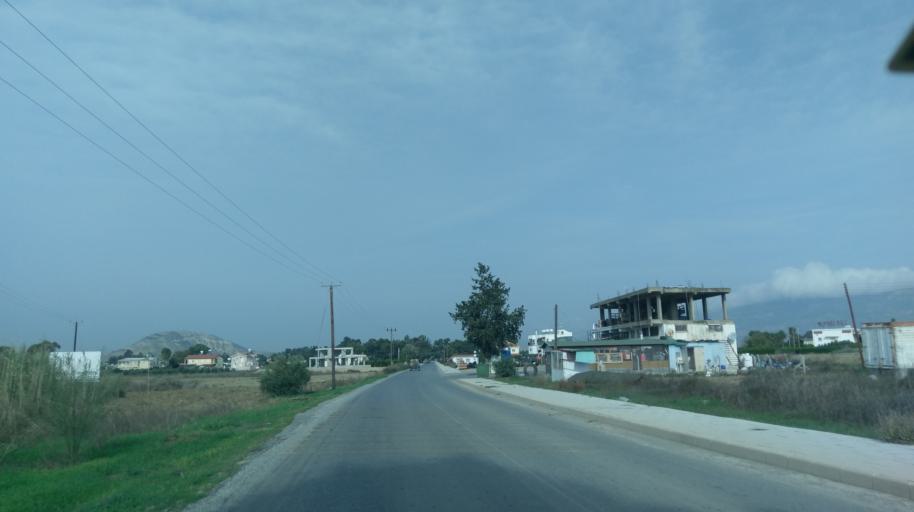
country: CY
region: Lefkosia
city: Mammari
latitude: 35.2260
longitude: 33.1725
